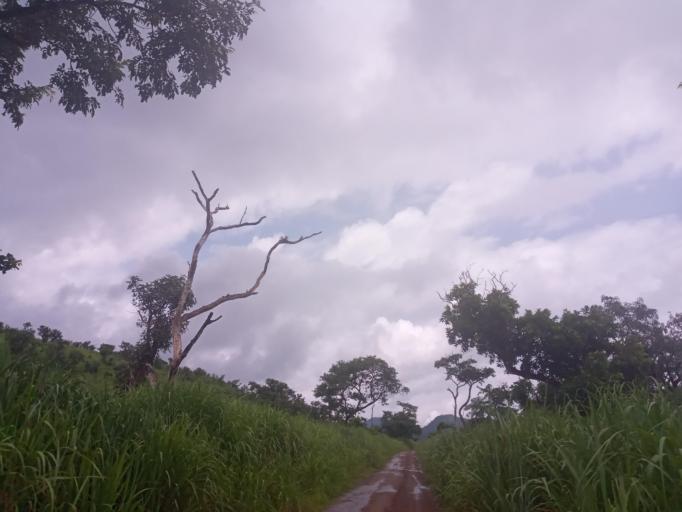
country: SL
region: Northern Province
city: Bumbuna
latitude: 8.9381
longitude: -11.7498
